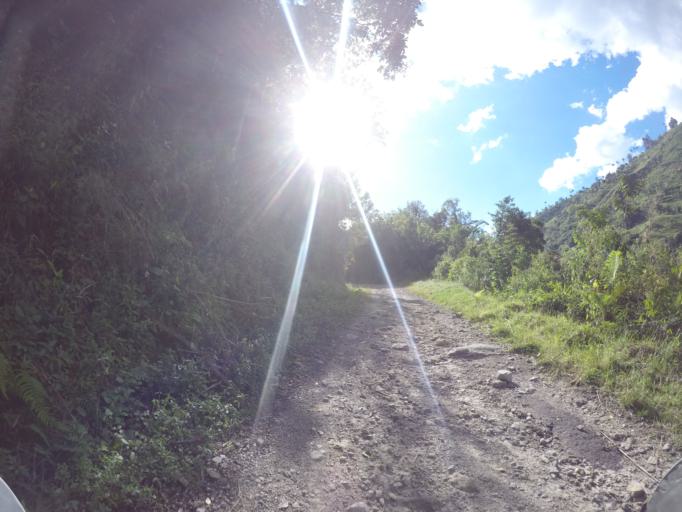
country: CO
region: Tolima
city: Cajamarca
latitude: 4.5043
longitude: -75.3936
